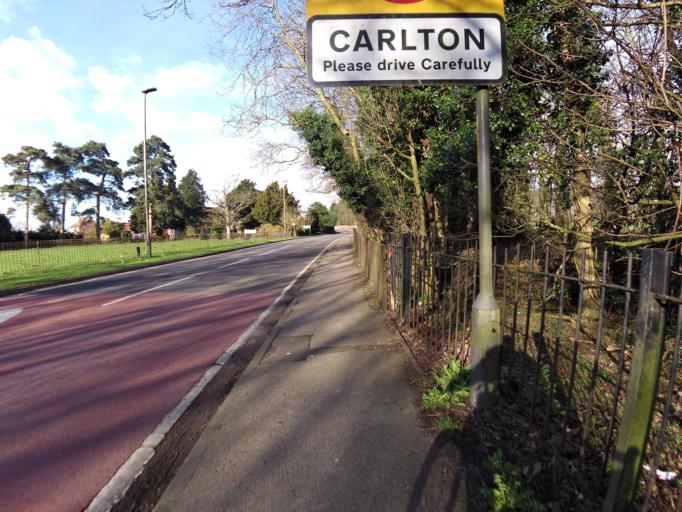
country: GB
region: England
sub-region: East Riding of Yorkshire
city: Snaith
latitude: 53.7032
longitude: -1.0216
